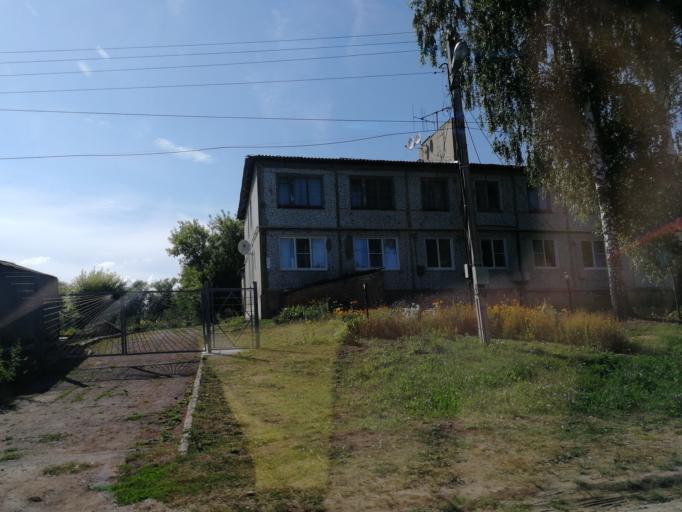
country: RU
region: Tula
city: Tovarkovskiy
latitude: 53.6131
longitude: 38.2697
